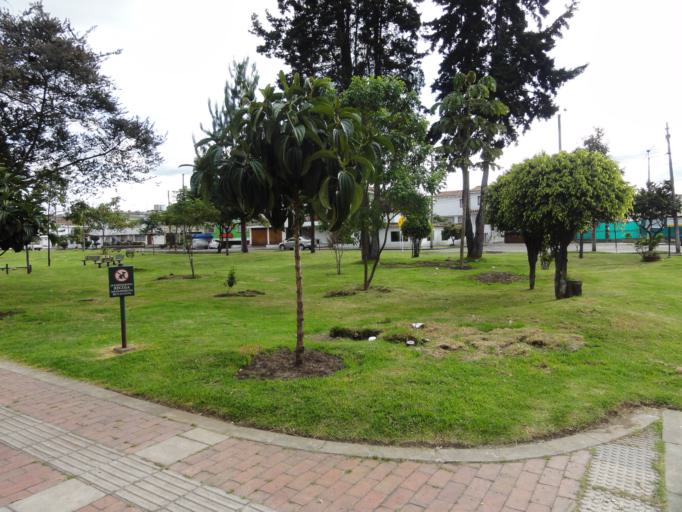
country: CO
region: Bogota D.C.
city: Bogota
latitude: 4.6489
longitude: -74.0792
